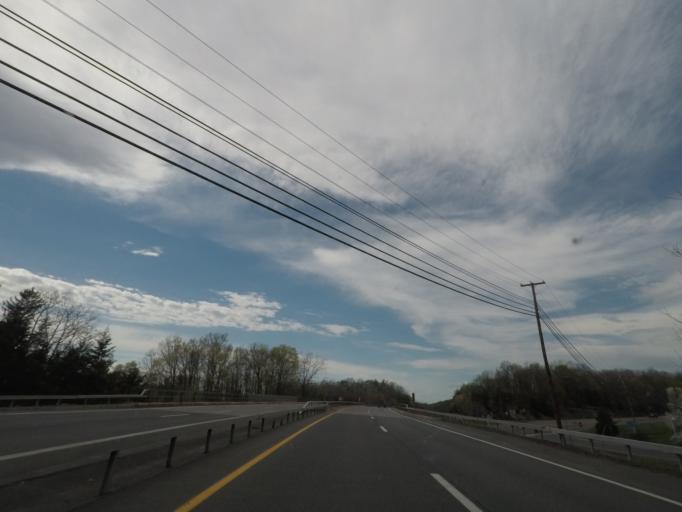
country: US
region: New York
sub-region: Greene County
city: Jefferson Heights
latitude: 42.2393
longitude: -73.8869
